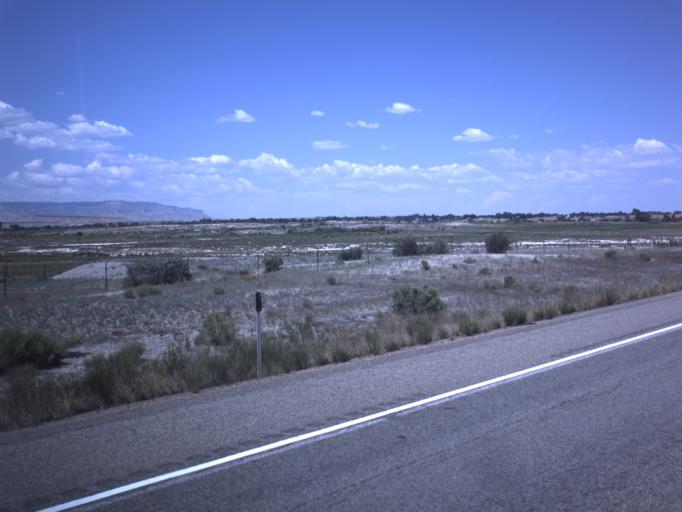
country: US
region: Utah
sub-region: Emery County
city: Castle Dale
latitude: 39.1865
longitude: -111.0312
